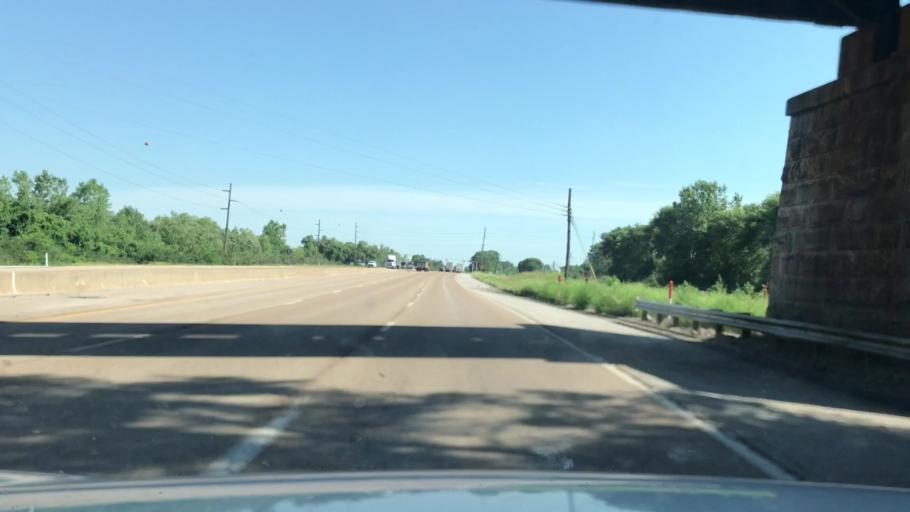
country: US
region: Illinois
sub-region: Madison County
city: Venice
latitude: 38.6767
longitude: -90.1739
